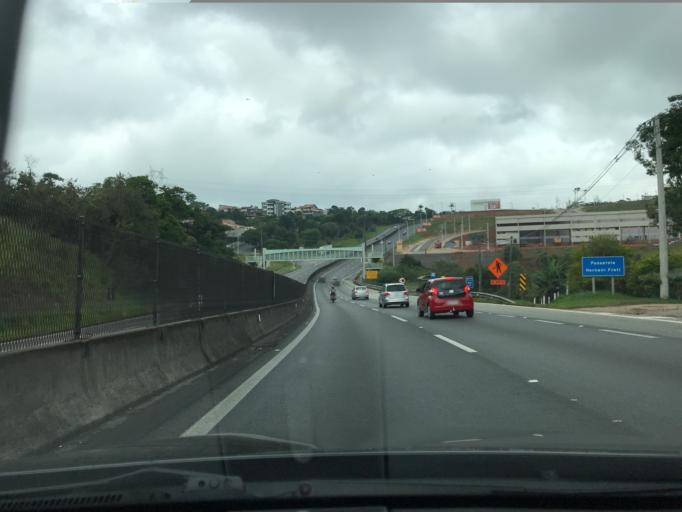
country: BR
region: Sao Paulo
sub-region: Cotia
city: Cotia
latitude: -23.6105
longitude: -46.9554
